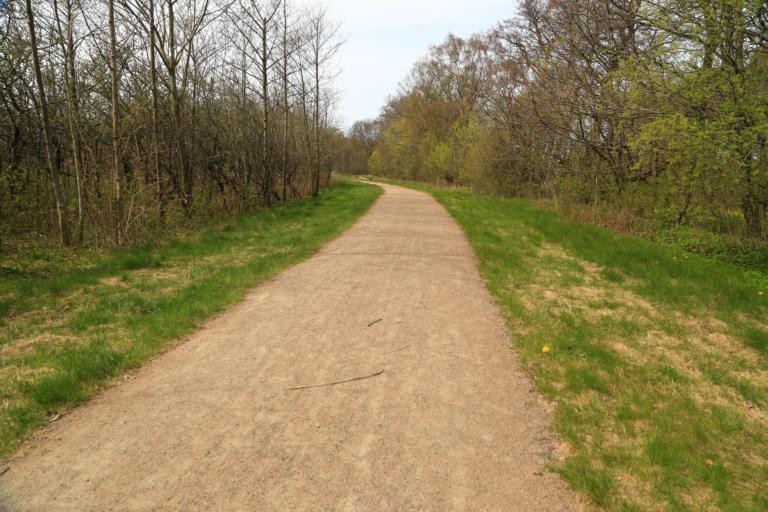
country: SE
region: Halland
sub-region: Varbergs Kommun
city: Varberg
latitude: 57.1332
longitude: 12.2772
